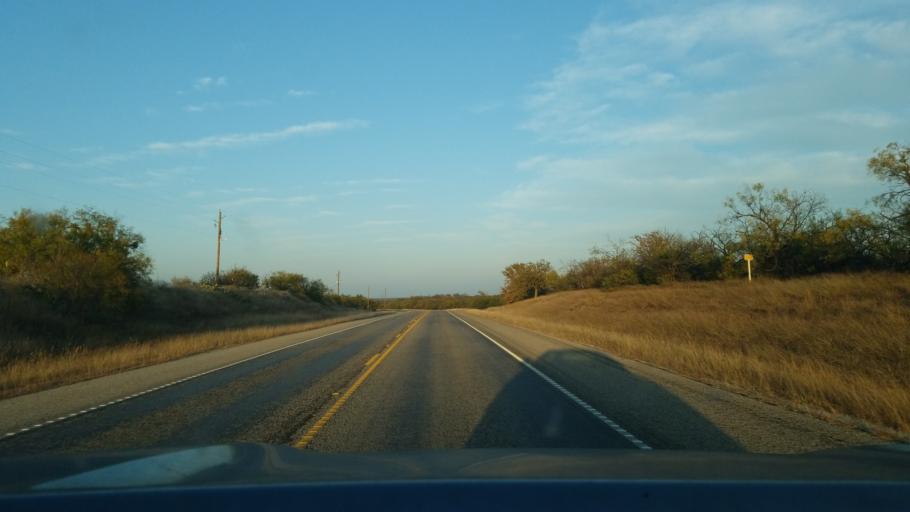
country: US
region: Texas
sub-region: Eastland County
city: Cisco
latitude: 32.4076
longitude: -98.9513
